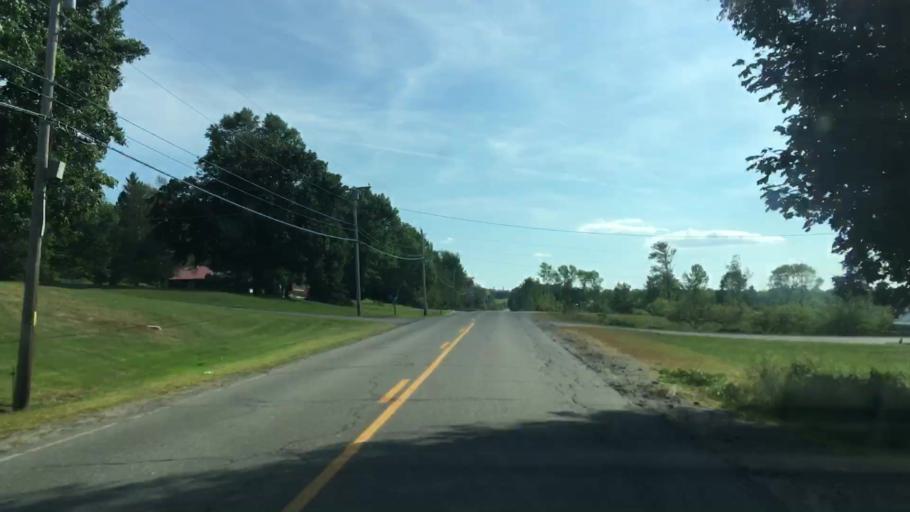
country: US
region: Maine
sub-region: Penobscot County
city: Lincoln
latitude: 45.3287
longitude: -68.5312
